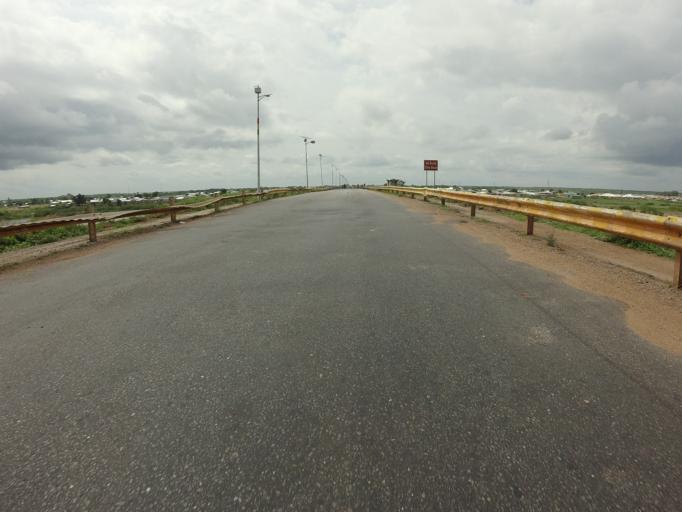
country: GH
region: Brong-Ahafo
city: Kintampo
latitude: 8.7642
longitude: -1.4547
